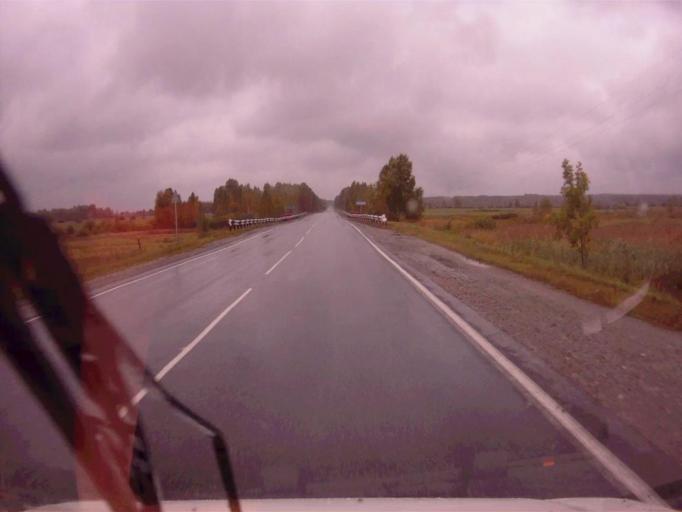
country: RU
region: Chelyabinsk
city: Argayash
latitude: 55.4793
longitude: 60.8095
